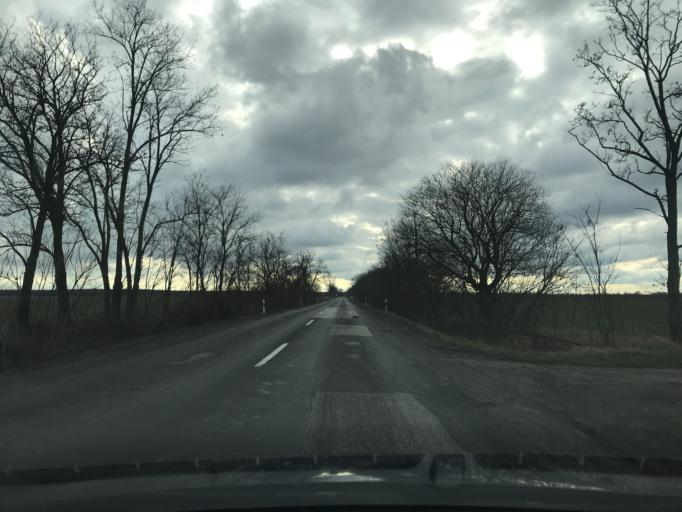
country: HU
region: Bacs-Kiskun
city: Csaszartoltes
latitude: 46.4086
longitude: 19.1703
